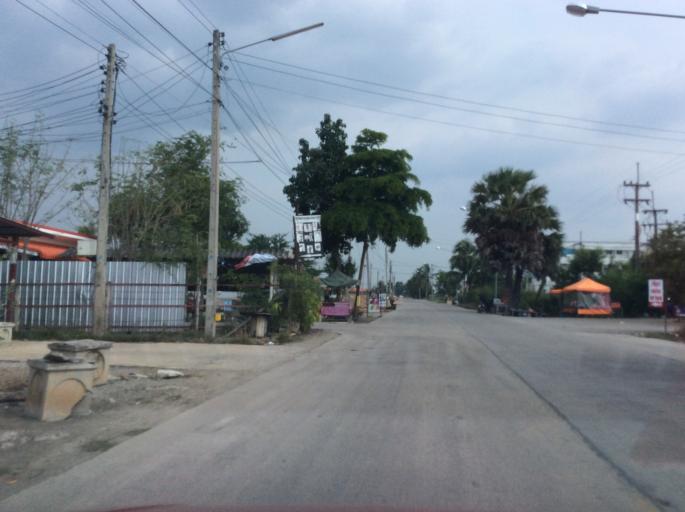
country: TH
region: Pathum Thani
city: Thanyaburi
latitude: 13.9864
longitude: 100.7274
